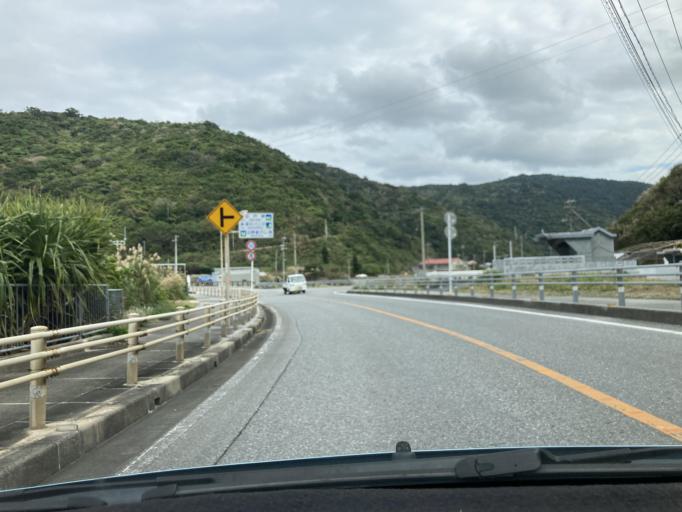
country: JP
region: Okinawa
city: Nago
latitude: 26.7971
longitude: 128.2314
